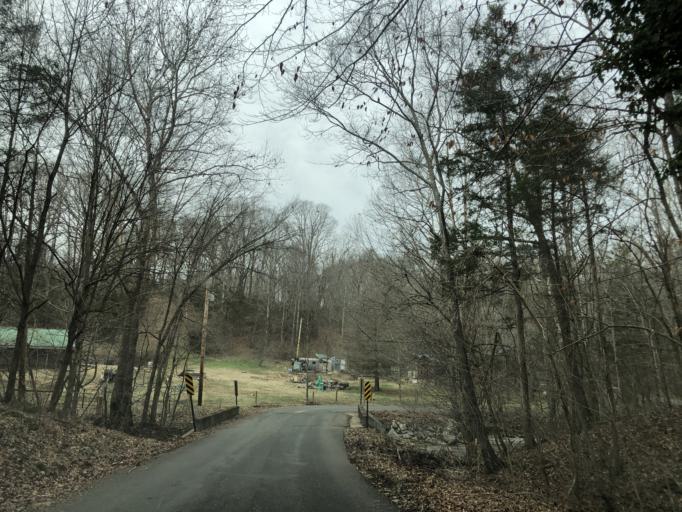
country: US
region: Tennessee
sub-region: Robertson County
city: Greenbrier
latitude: 36.4668
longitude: -86.7908
